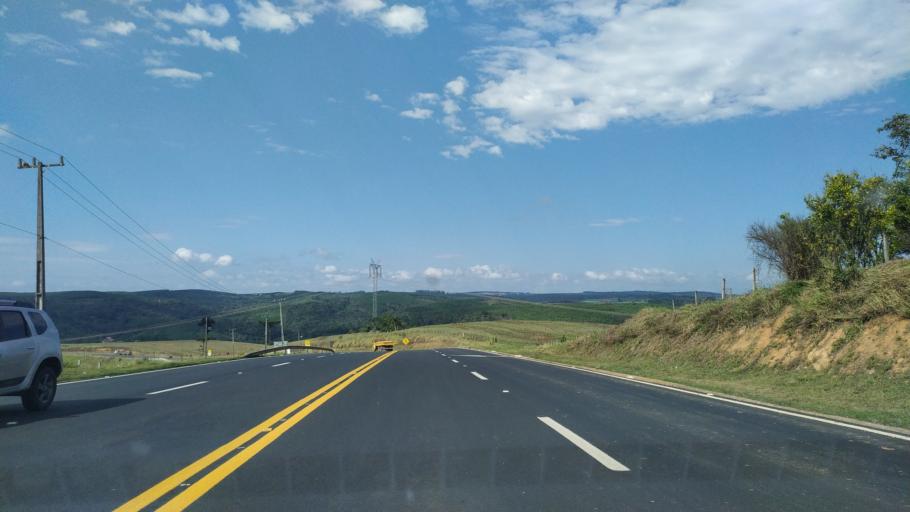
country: BR
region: Parana
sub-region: Telemaco Borba
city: Telemaco Borba
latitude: -24.2827
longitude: -50.7131
